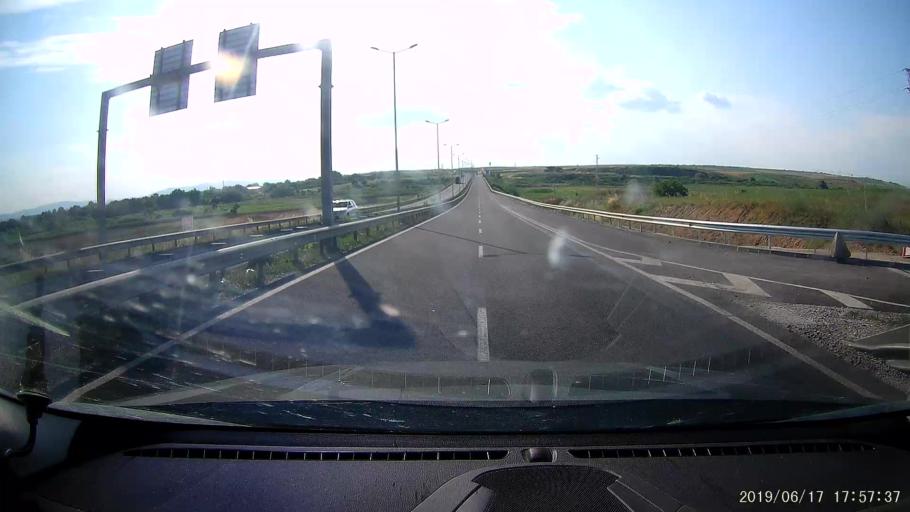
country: GR
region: East Macedonia and Thrace
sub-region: Nomos Evrou
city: Rizia
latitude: 41.7221
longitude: 26.3328
